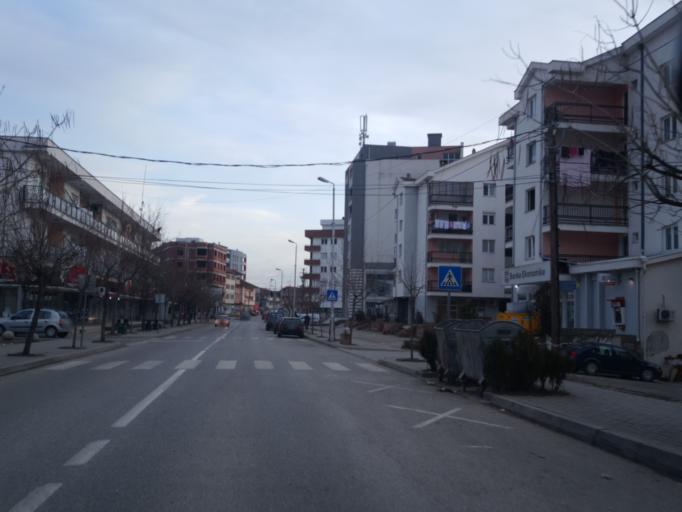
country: XK
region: Pec
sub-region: Komuna e Istogut
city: Istok
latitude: 42.7803
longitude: 20.4869
